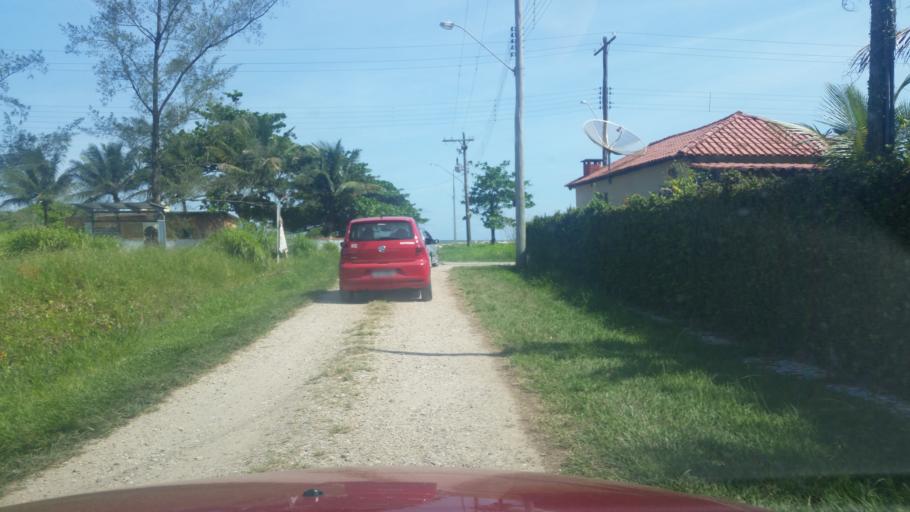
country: BR
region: Sao Paulo
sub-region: Iguape
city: Iguape
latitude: -24.6960
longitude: -47.4520
